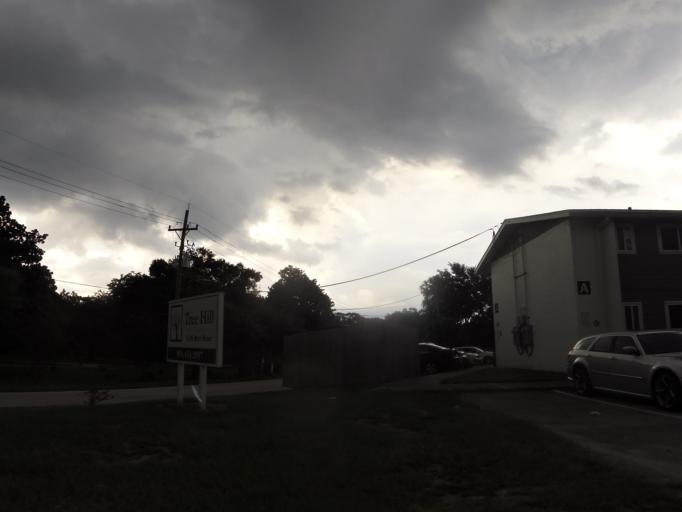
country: US
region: Florida
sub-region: Duval County
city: Jacksonville
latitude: 30.3327
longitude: -81.5874
